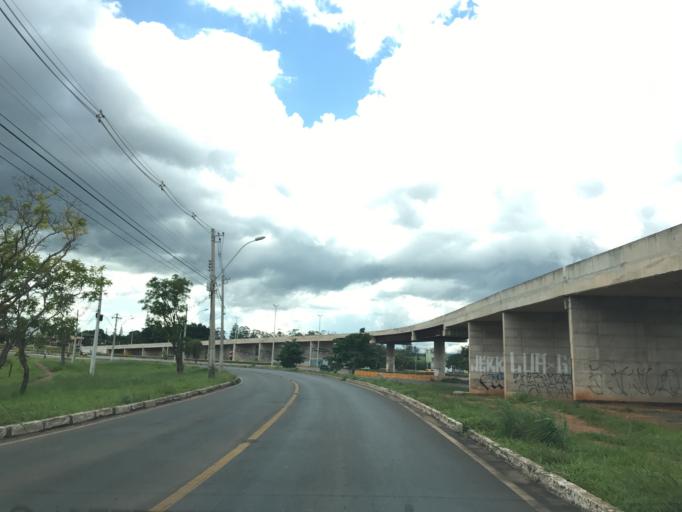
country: BR
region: Federal District
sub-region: Brasilia
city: Brasilia
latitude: -15.8759
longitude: -47.9579
